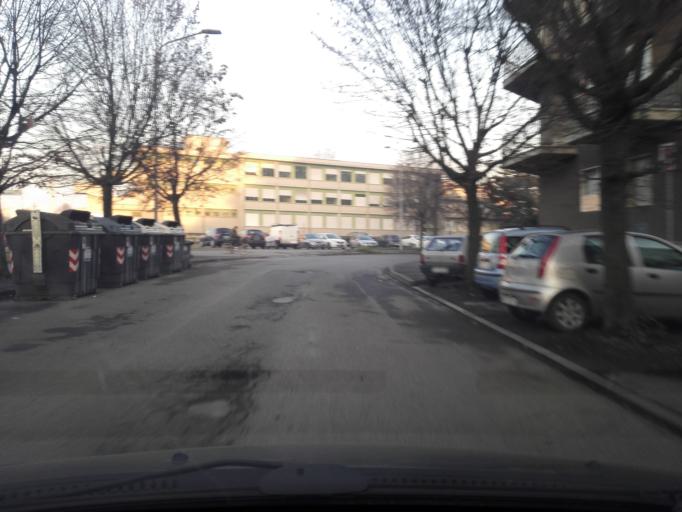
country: IT
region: Piedmont
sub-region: Provincia di Alessandria
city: Alessandria
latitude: 44.8969
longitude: 8.6019
